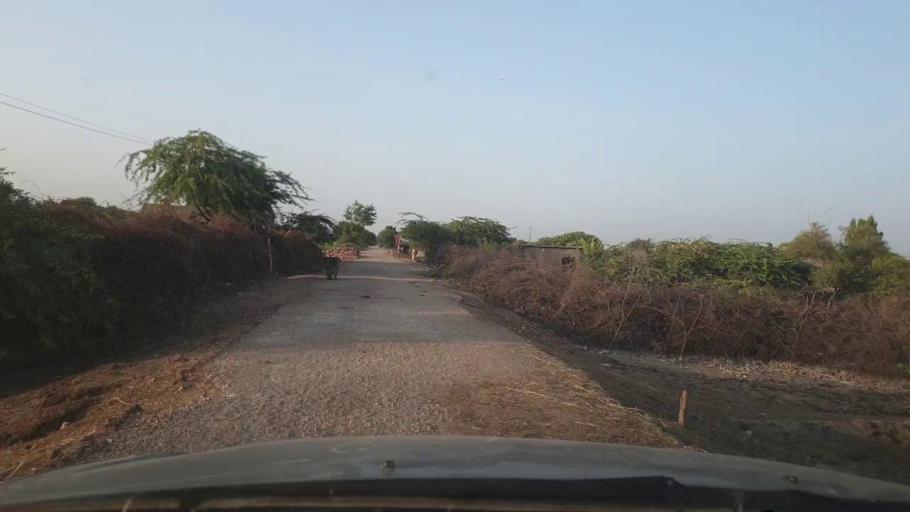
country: PK
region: Sindh
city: Tando Ghulam Ali
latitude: 25.1549
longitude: 68.9747
